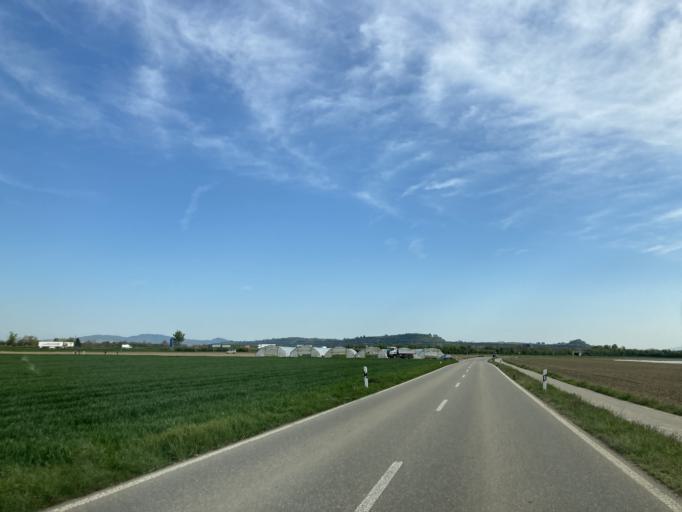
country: DE
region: Baden-Wuerttemberg
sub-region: Freiburg Region
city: Hartheim
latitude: 47.9457
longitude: 7.6579
